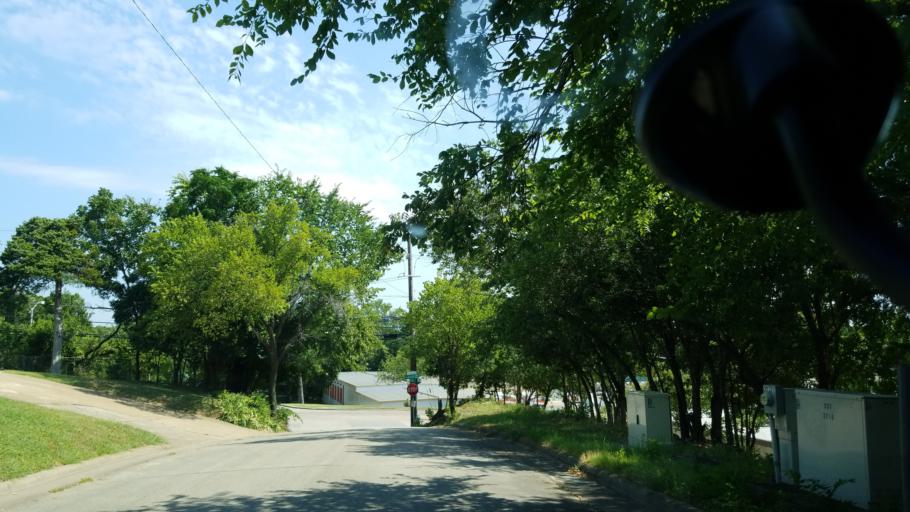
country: US
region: Texas
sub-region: Dallas County
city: Cockrell Hill
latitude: 32.7052
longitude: -96.8762
